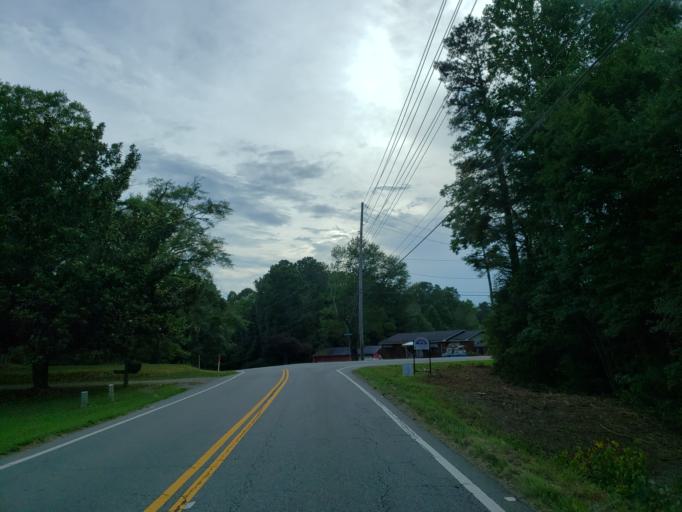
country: US
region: Georgia
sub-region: Cherokee County
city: Holly Springs
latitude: 34.1221
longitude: -84.4211
